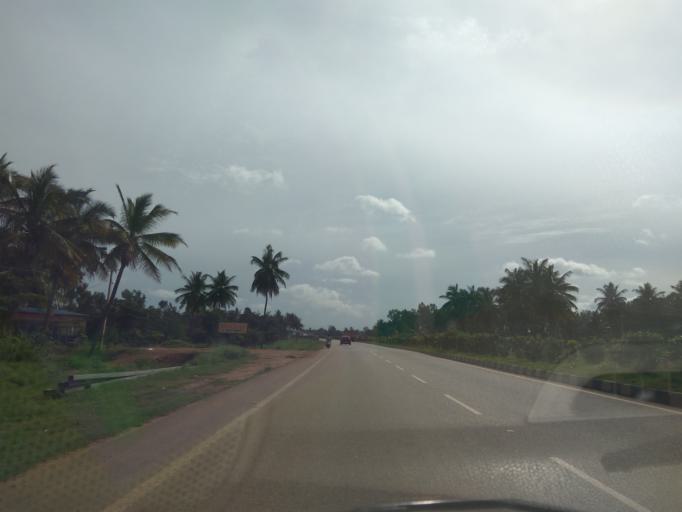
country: IN
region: Karnataka
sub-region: Bangalore Rural
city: Dasarahalli
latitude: 13.0995
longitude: 77.8604
